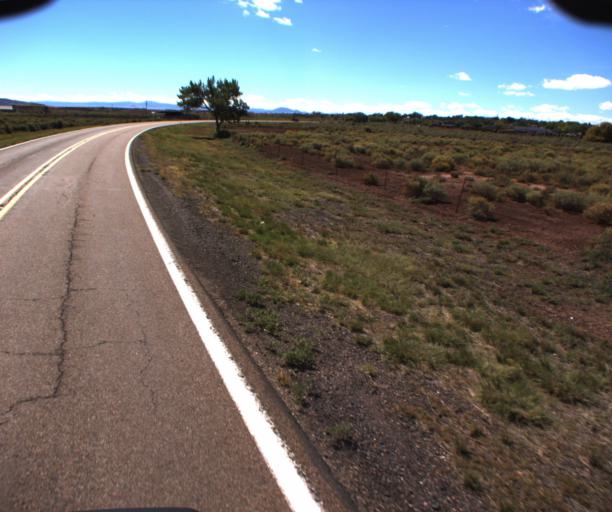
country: US
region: Arizona
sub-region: Apache County
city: Saint Johns
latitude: 34.5100
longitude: -109.3484
